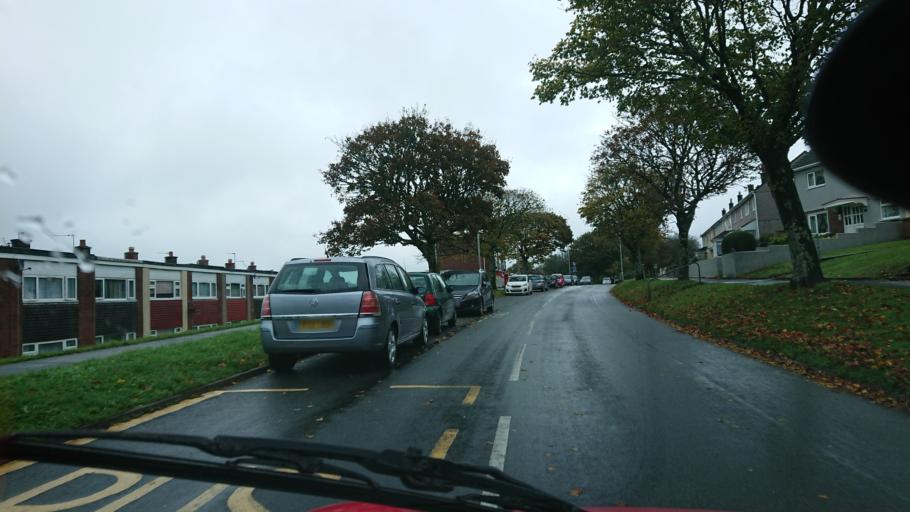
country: GB
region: England
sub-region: Plymouth
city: Plymouth
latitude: 50.4303
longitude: -4.1327
